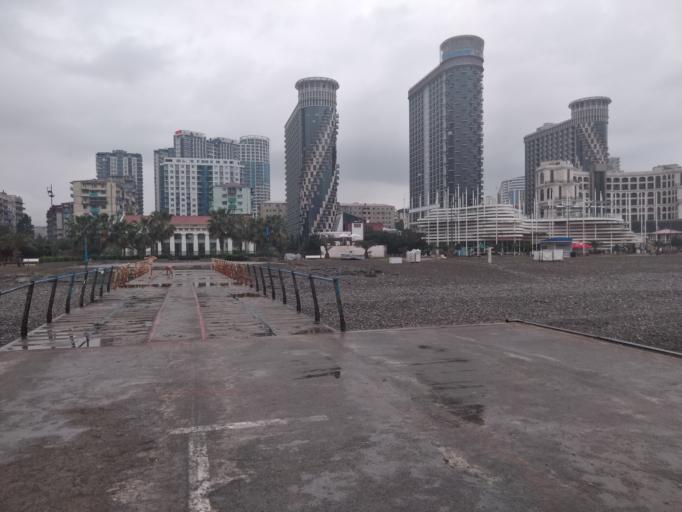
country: GE
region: Ajaria
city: Batumi
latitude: 41.6398
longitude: 41.6090
